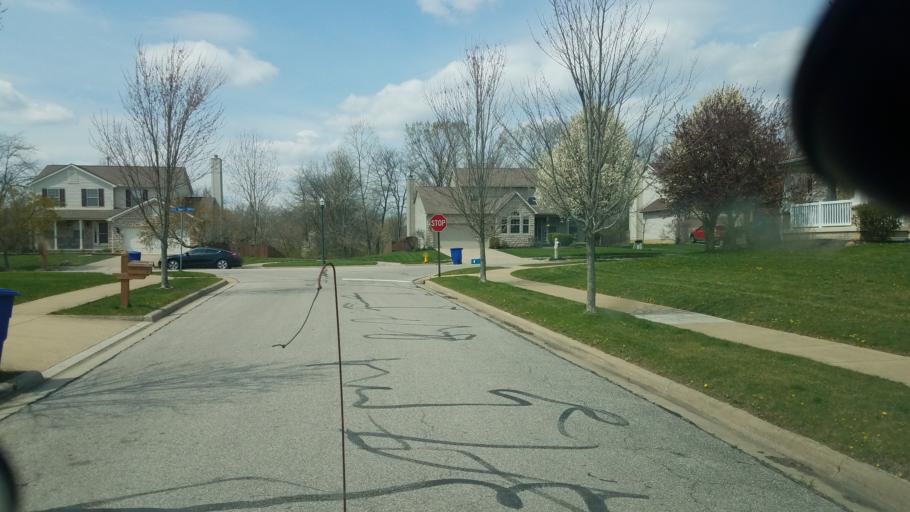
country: US
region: Ohio
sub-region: Delaware County
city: Delaware
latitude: 40.3080
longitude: -83.1175
